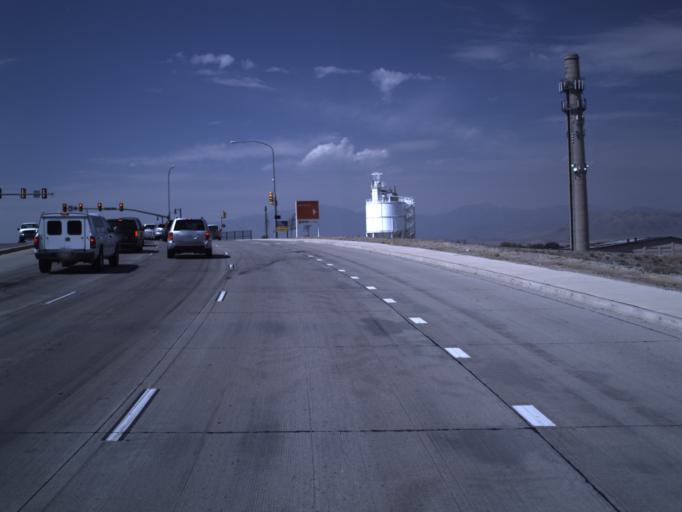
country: US
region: Utah
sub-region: Utah County
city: Lehi
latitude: 40.3778
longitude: -111.8308
